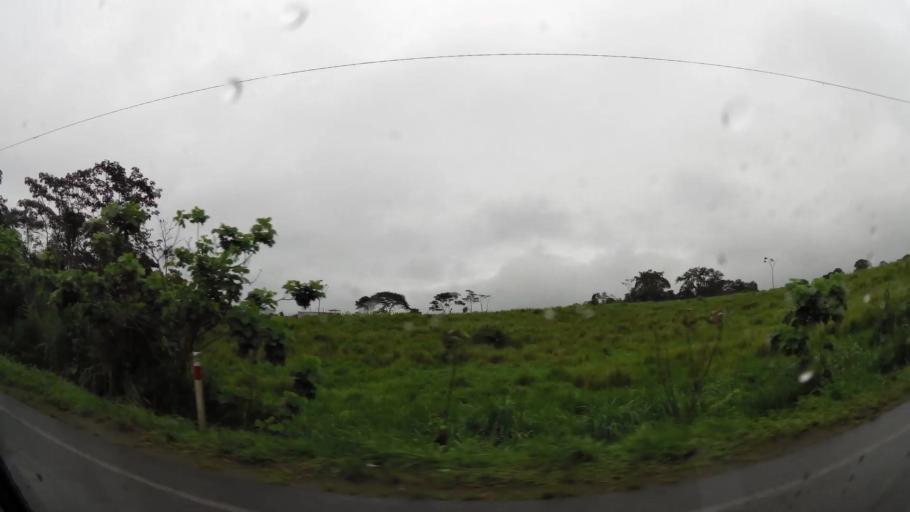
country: EC
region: Santo Domingo de los Tsachilas
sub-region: Canton Santo Domingo de los Colorados
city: Santo Domingo de los Colorados
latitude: -0.2324
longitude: -79.1604
